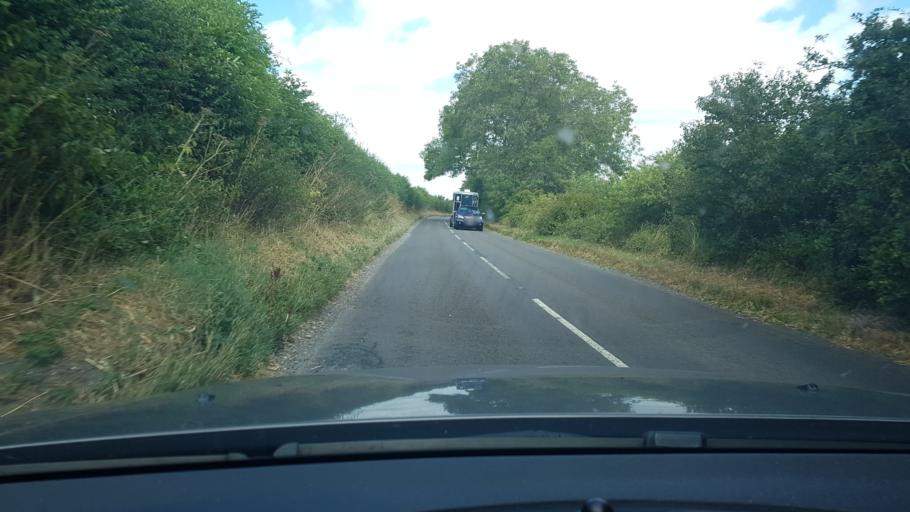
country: GB
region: England
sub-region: Wiltshire
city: Shalbourne
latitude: 51.3658
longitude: -1.5590
